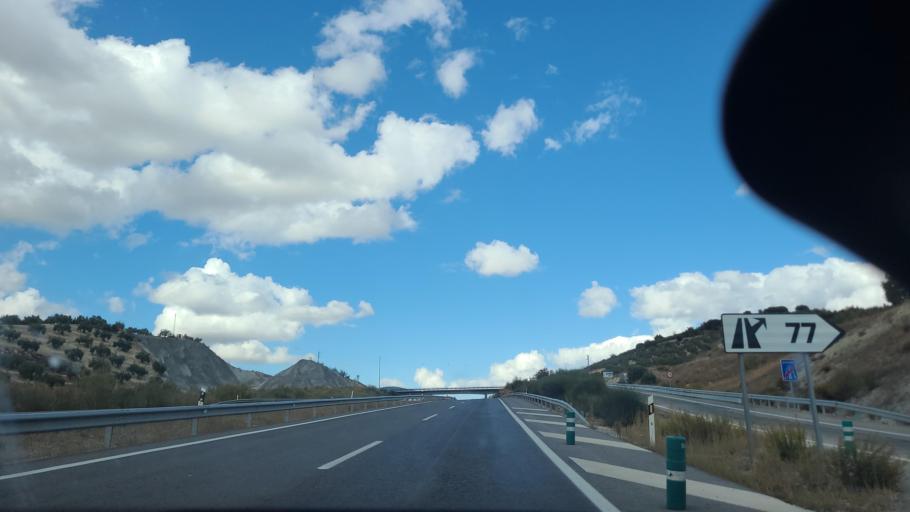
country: ES
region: Andalusia
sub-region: Provincia de Jaen
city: Noalejo
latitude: 37.5294
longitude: -3.6364
